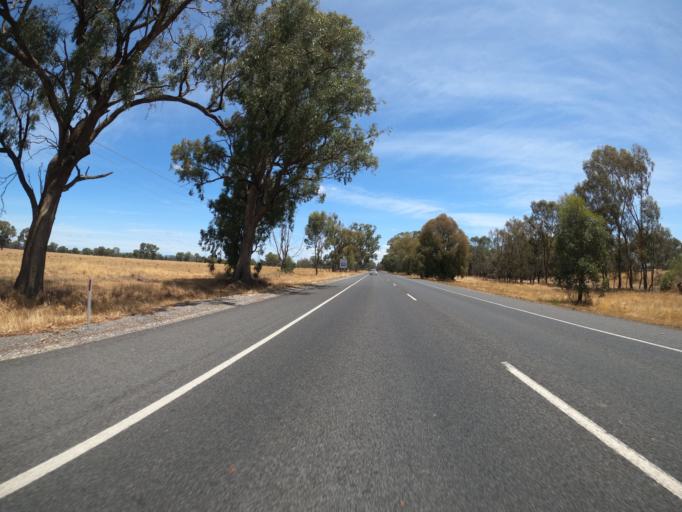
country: AU
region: Victoria
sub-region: Benalla
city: Benalla
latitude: -36.5283
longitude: 146.0456
